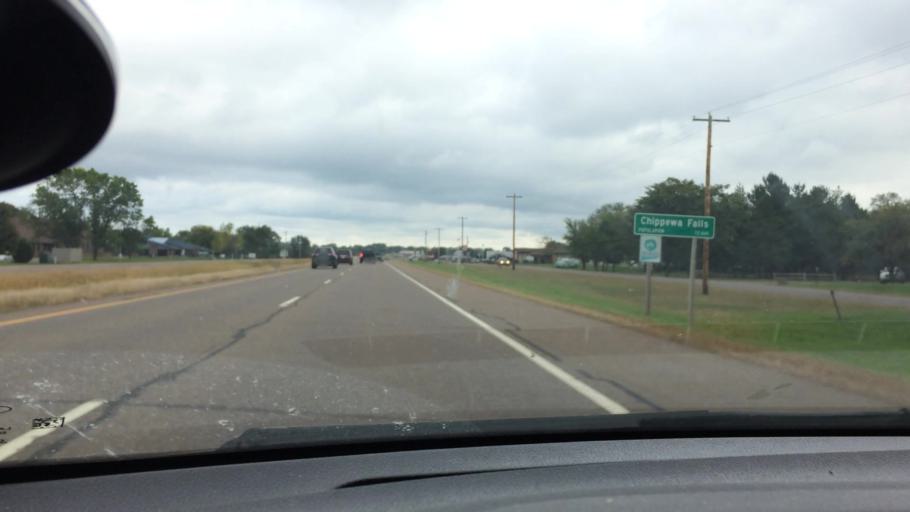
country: US
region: Wisconsin
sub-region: Chippewa County
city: Chippewa Falls
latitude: 44.9123
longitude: -91.3983
